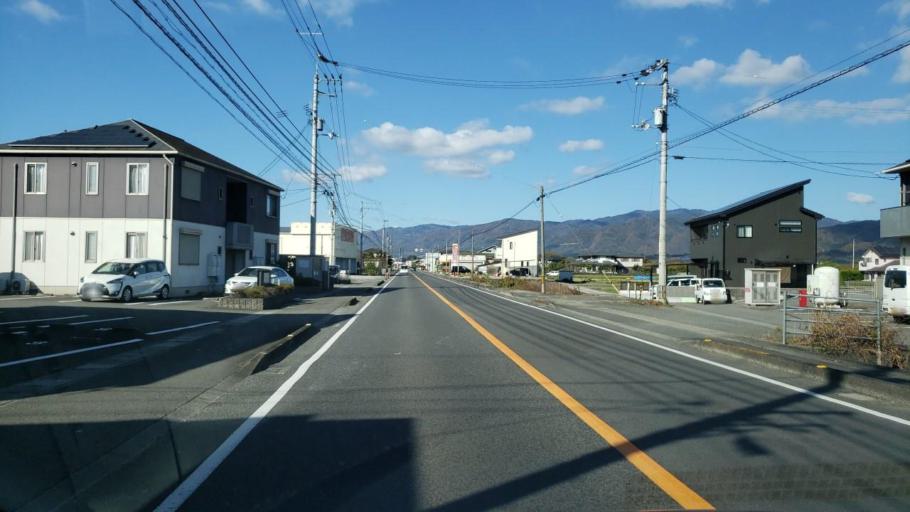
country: JP
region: Tokushima
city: Wakimachi
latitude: 34.0588
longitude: 134.2195
